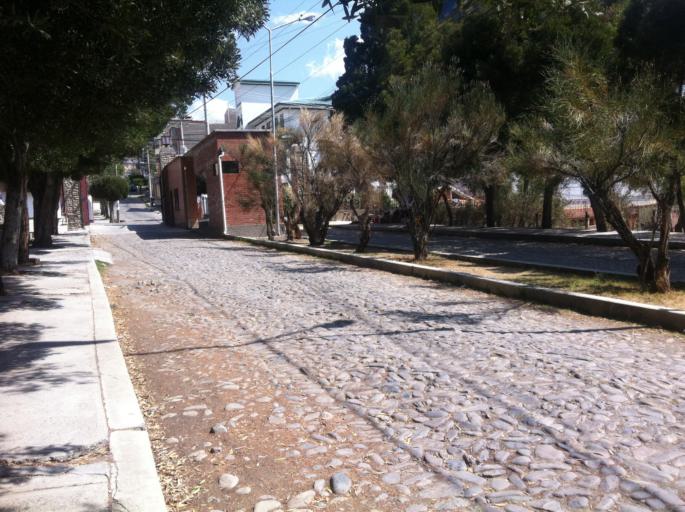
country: BO
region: La Paz
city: La Paz
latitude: -16.5392
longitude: -68.0682
